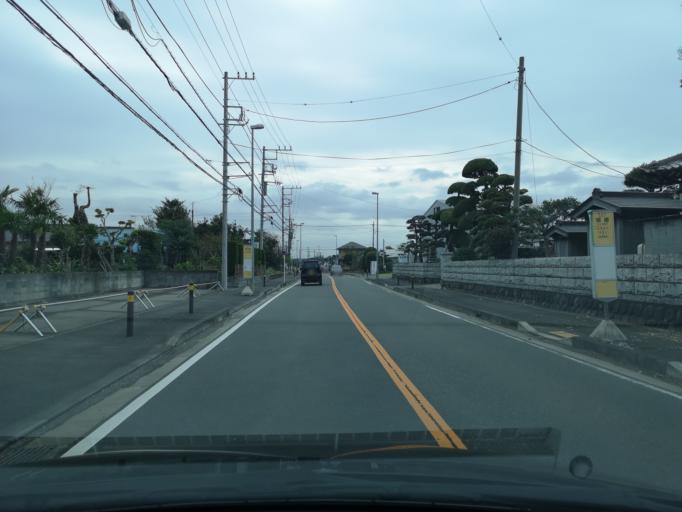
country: JP
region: Kanagawa
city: Chigasaki
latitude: 35.3891
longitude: 139.4042
